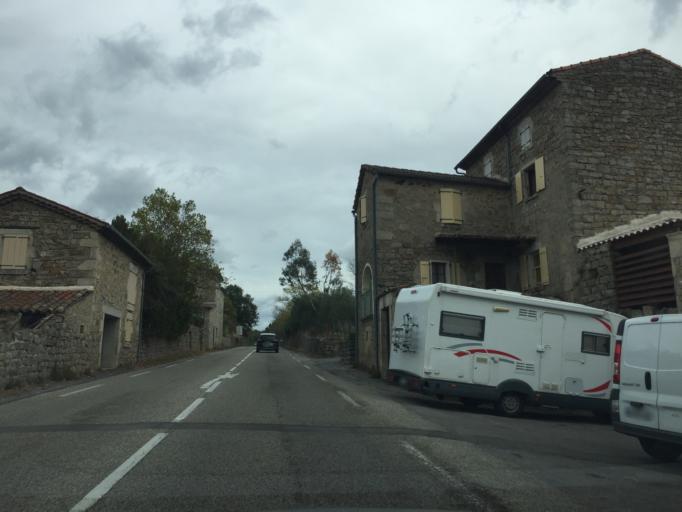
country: FR
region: Rhone-Alpes
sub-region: Departement de l'Ardeche
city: Lablachere
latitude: 44.4328
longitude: 4.1902
